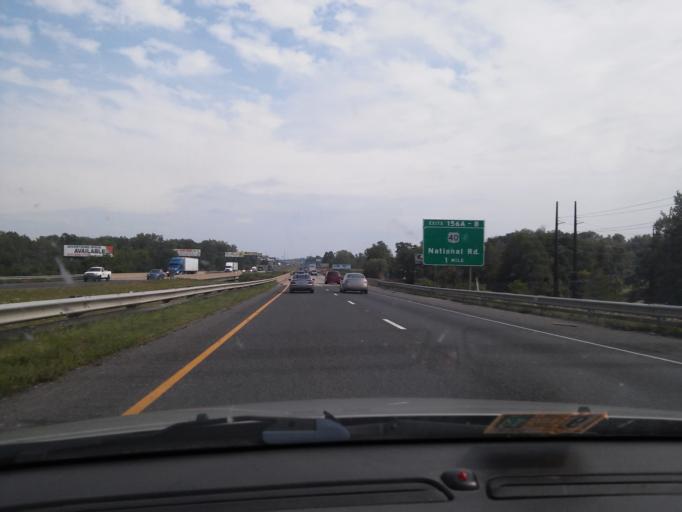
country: US
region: Ohio
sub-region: Preble County
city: New Paris
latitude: 39.8482
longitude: -84.8329
